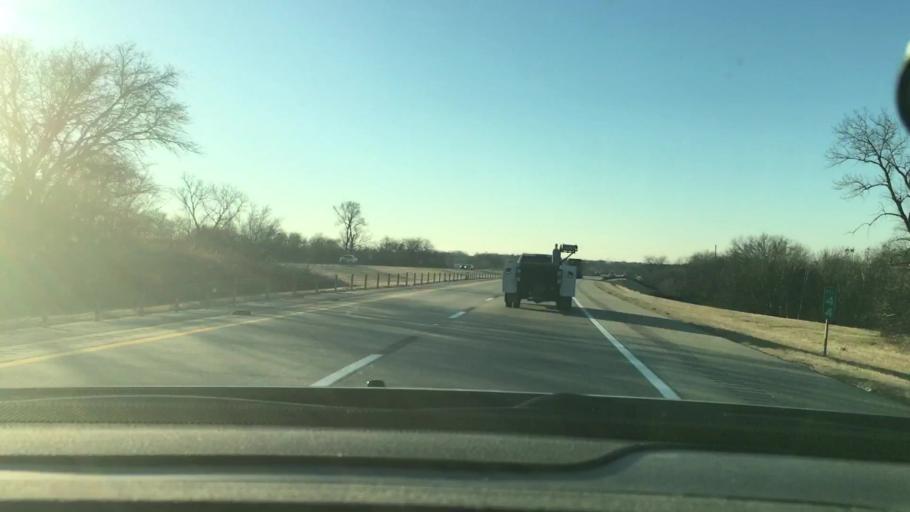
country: US
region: Oklahoma
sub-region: Murray County
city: Davis
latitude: 34.3502
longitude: -97.1483
